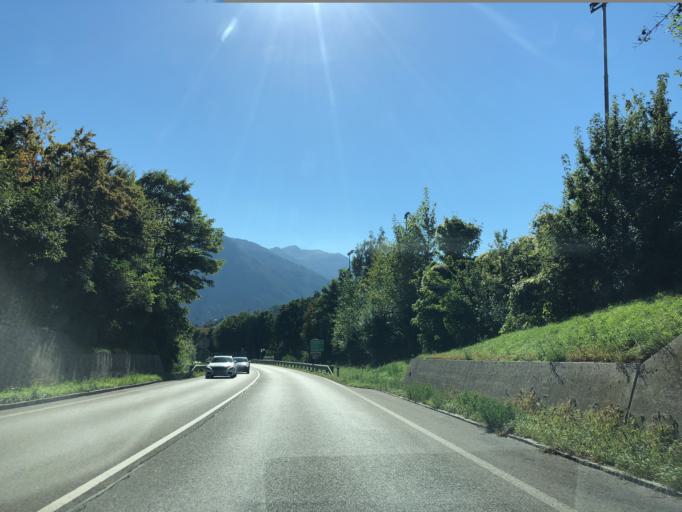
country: AT
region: Tyrol
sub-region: Politischer Bezirk Imst
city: Imst
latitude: 47.2438
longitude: 10.7442
